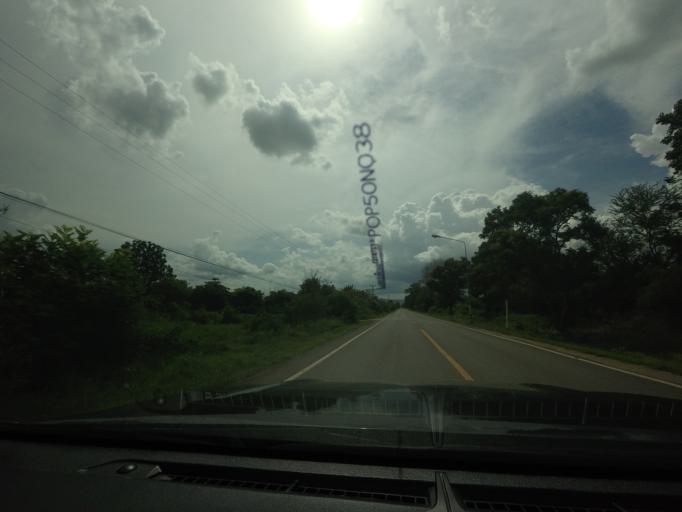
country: TH
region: Kanchanaburi
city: Bo Phloi
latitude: 14.1659
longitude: 99.4592
